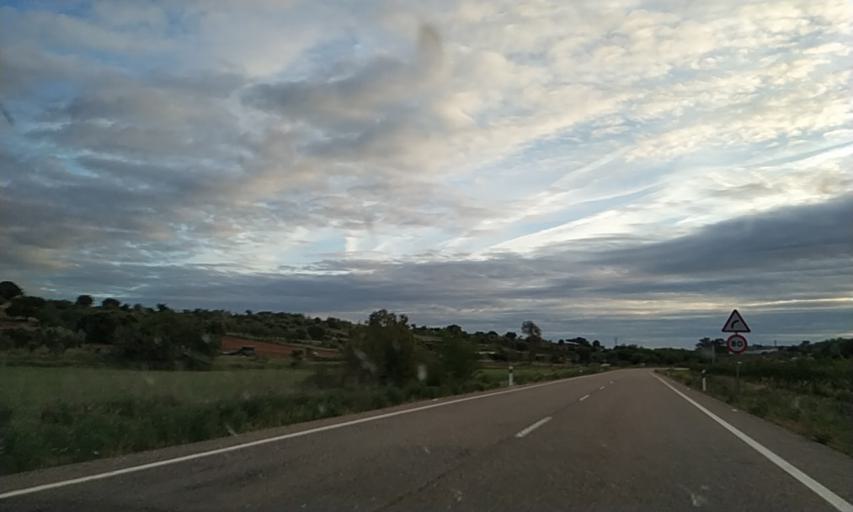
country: ES
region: Extremadura
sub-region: Provincia de Badajoz
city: La Roca de la Sierra
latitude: 39.1189
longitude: -6.6779
